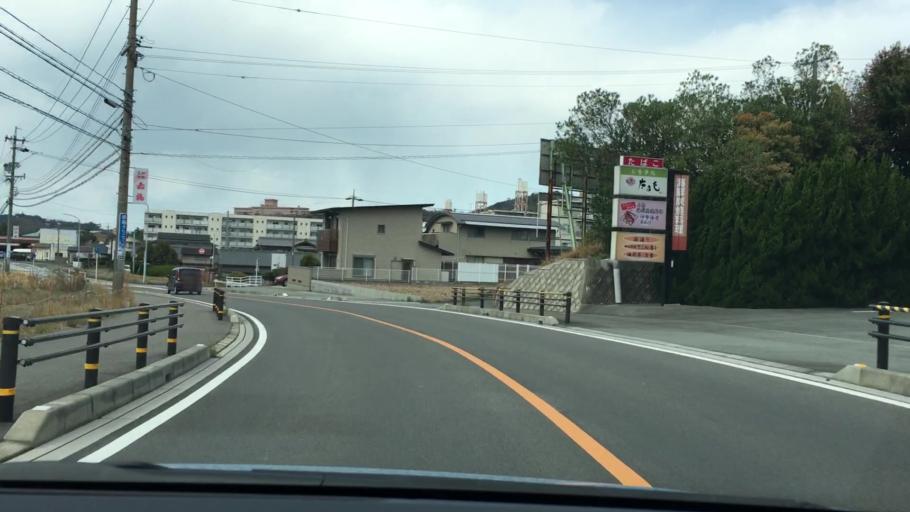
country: JP
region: Mie
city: Toba
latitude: 34.4657
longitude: 136.8549
